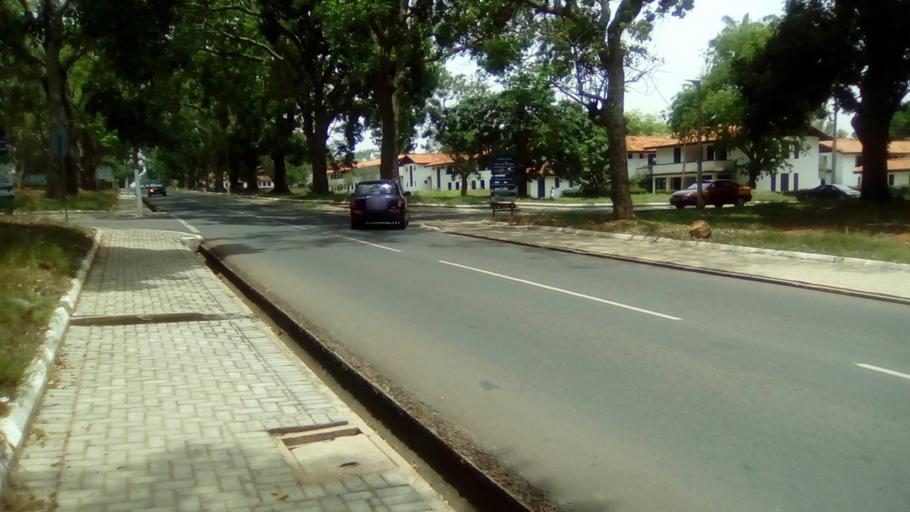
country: GH
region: Greater Accra
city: Medina Estates
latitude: 5.6479
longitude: -0.1892
